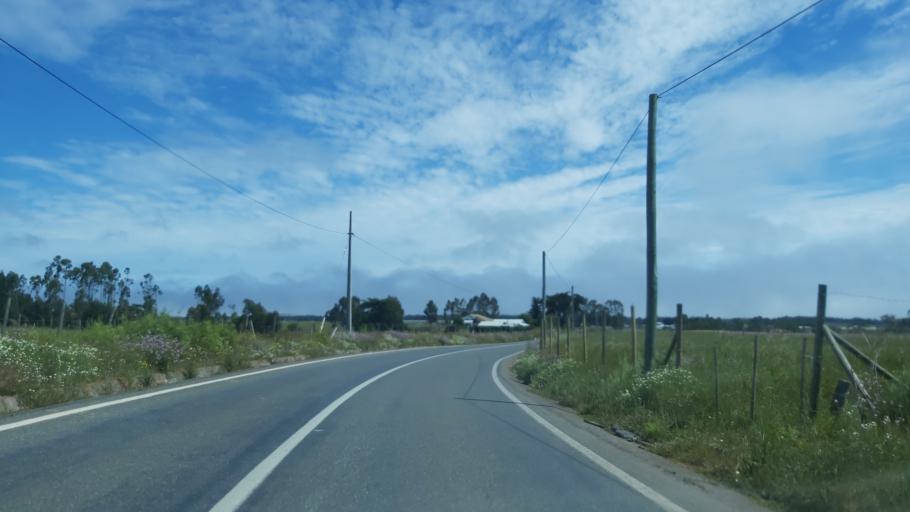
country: CL
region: Maule
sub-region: Provincia de Talca
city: Constitucion
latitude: -35.5828
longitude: -72.6018
